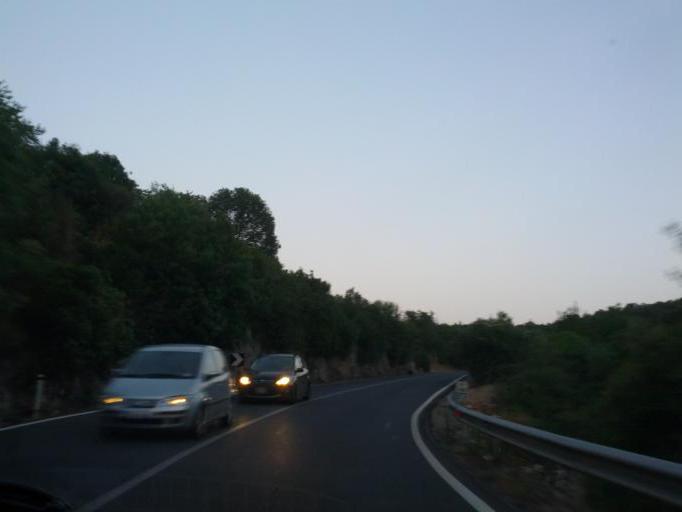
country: IT
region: Latium
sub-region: Provincia di Latina
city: Itri
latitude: 41.3088
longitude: 13.4934
